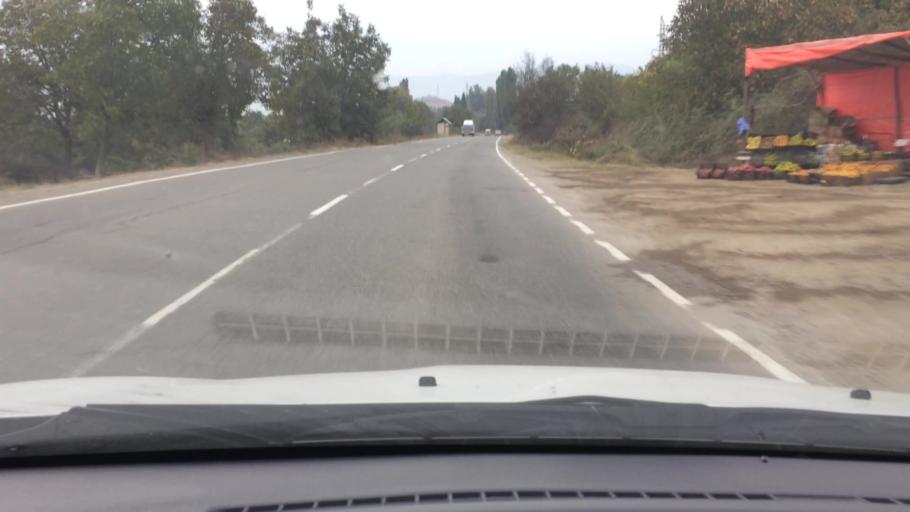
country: GE
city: Naghvarevi
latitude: 41.3020
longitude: 44.7896
